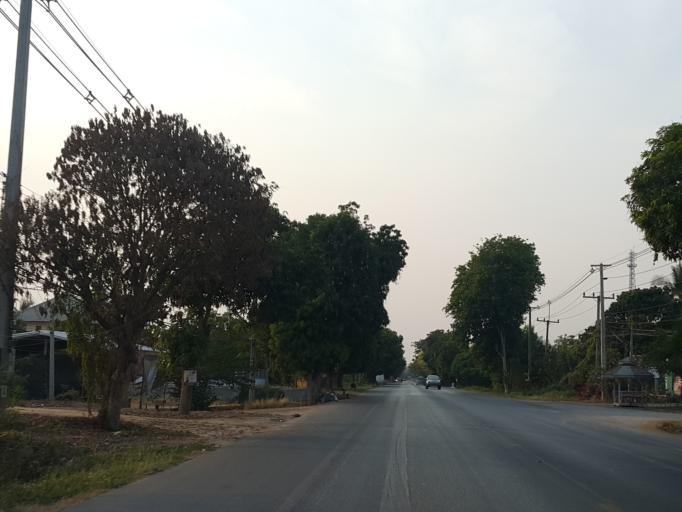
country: TH
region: Sukhothai
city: Si Samrong
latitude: 17.2192
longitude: 99.8628
